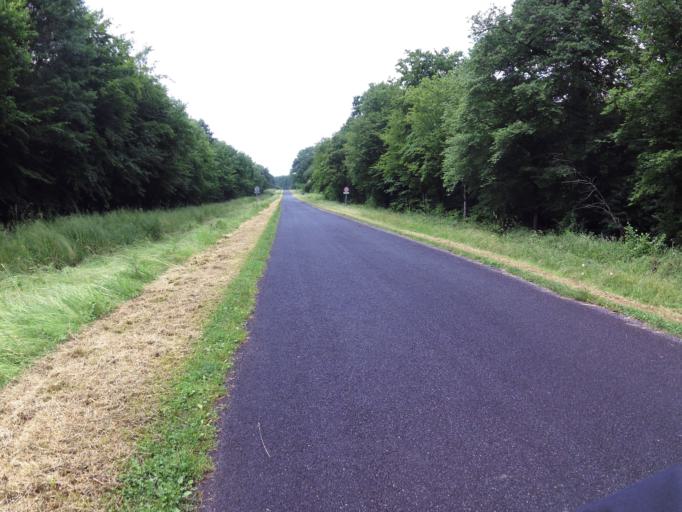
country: FR
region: Champagne-Ardenne
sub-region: Departement de la Marne
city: Sermaize-les-Bains
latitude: 48.7692
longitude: 4.9372
